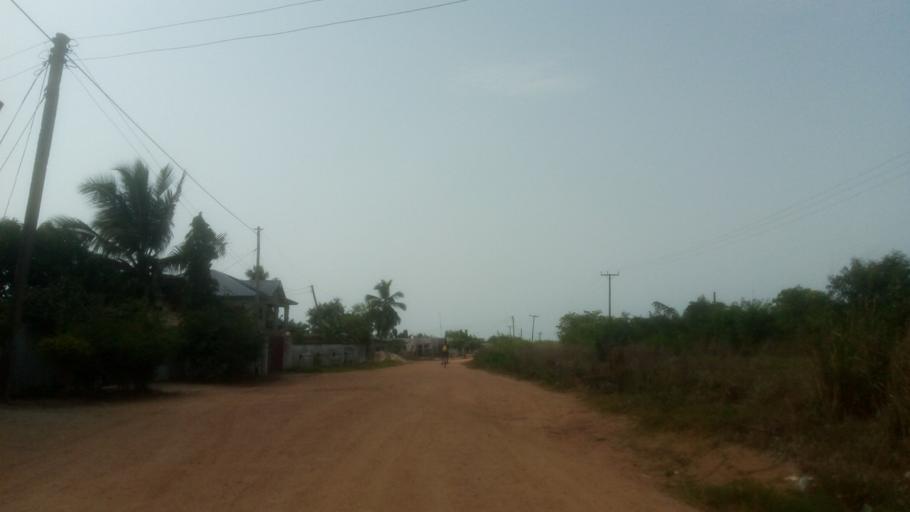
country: GH
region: Central
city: Winneba
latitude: 5.3561
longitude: -0.6360
